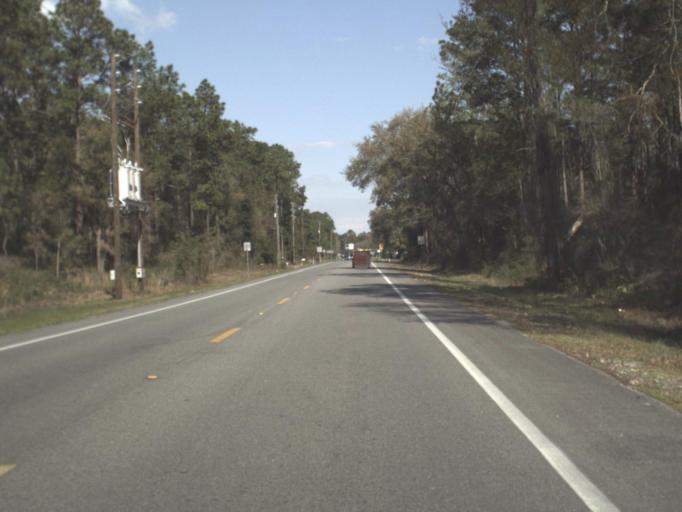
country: US
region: Florida
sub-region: Wakulla County
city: Crawfordville
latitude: 30.0806
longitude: -84.3949
